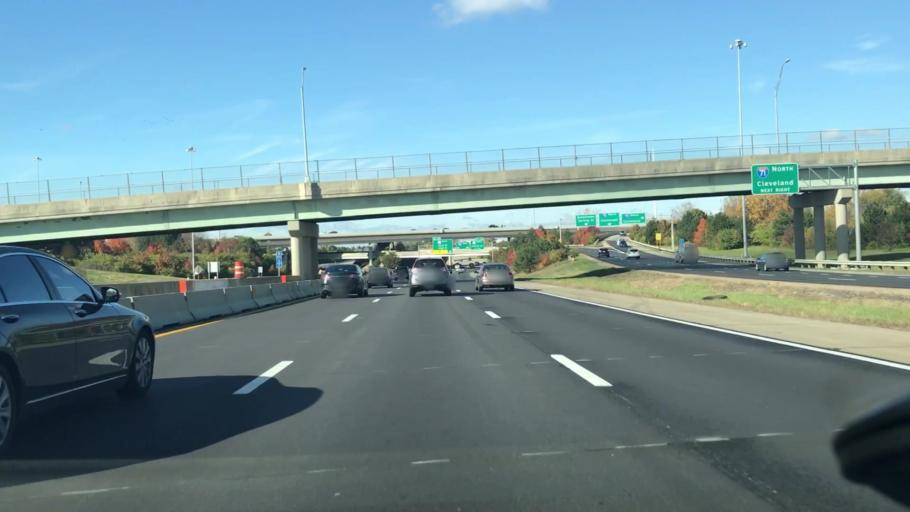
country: US
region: Ohio
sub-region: Franklin County
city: Columbus
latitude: 39.9787
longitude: -82.9796
